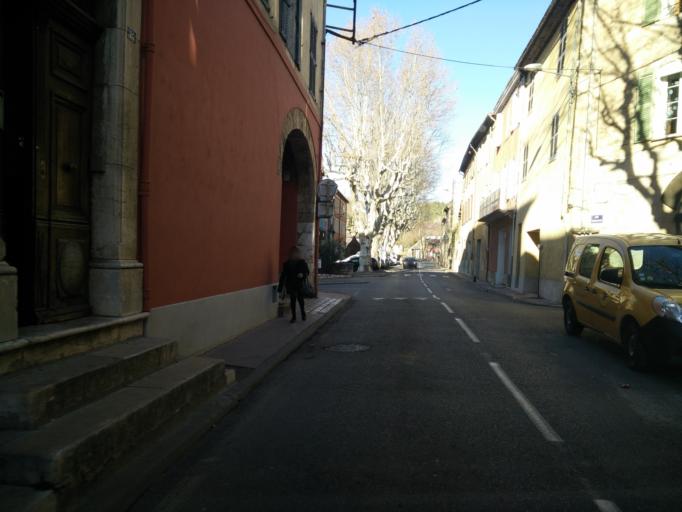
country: FR
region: Provence-Alpes-Cote d'Azur
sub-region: Departement du Var
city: Salernes
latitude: 43.5645
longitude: 6.2306
